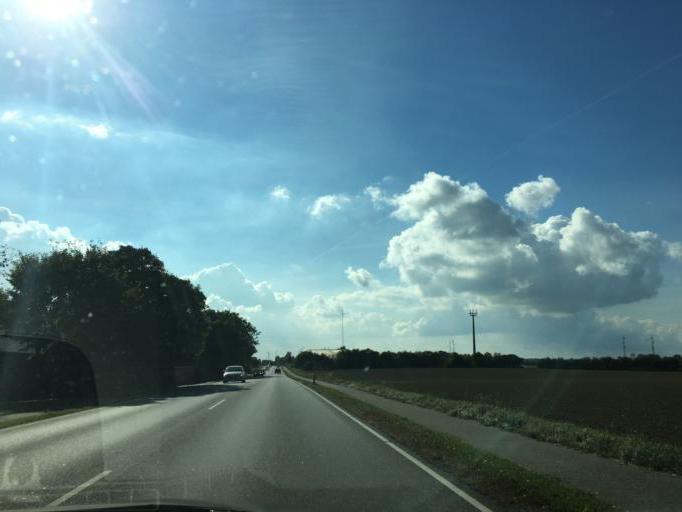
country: DK
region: South Denmark
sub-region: Fredericia Kommune
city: Snoghoj
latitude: 55.5647
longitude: 9.6821
